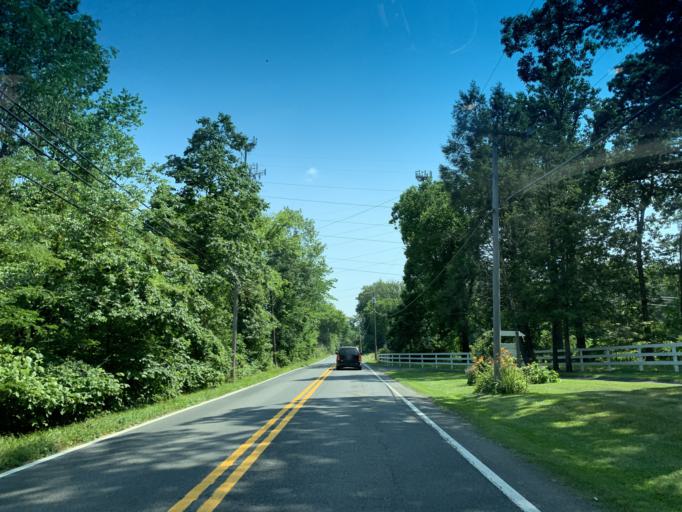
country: US
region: Maryland
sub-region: Montgomery County
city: Poolesville
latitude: 39.1858
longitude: -77.4054
